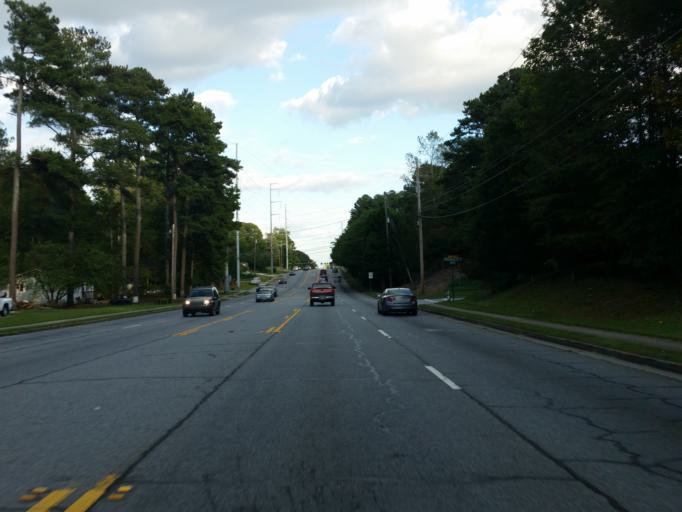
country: US
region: Georgia
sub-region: Cobb County
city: Fair Oaks
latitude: 33.8950
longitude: -84.5709
